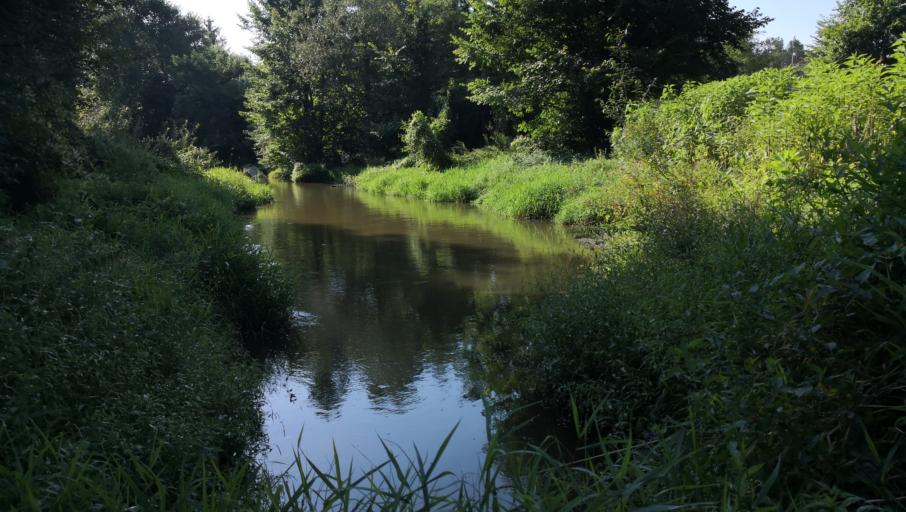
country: PL
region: Subcarpathian Voivodeship
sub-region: Powiat stalowowolski
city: Chwalowice
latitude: 50.7722
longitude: 21.9708
